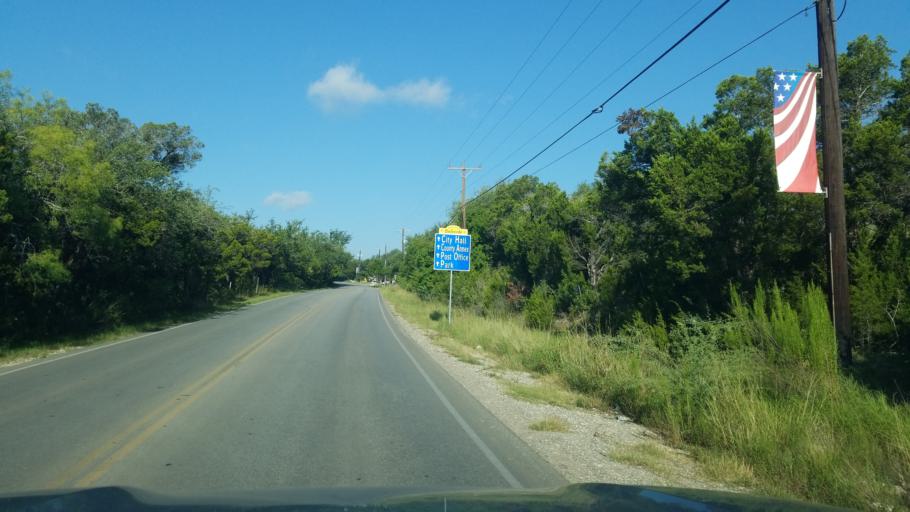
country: US
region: Texas
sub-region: Comal County
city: Bulverde
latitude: 29.7424
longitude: -98.4383
